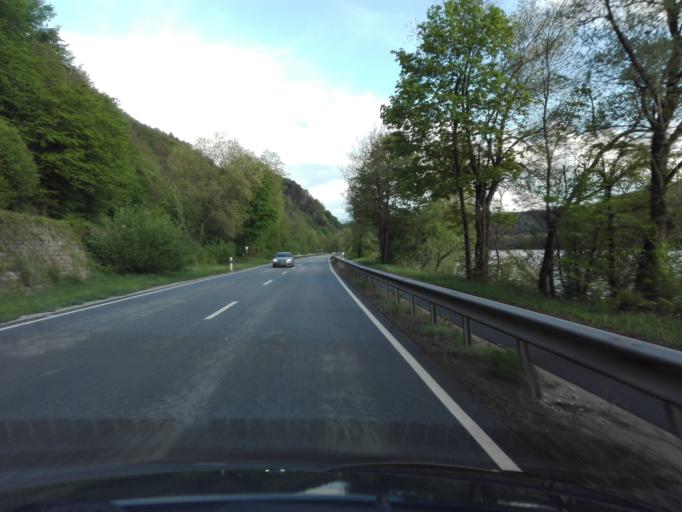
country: DE
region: Bavaria
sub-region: Lower Bavaria
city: Thyrnau
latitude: 48.5805
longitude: 13.5394
